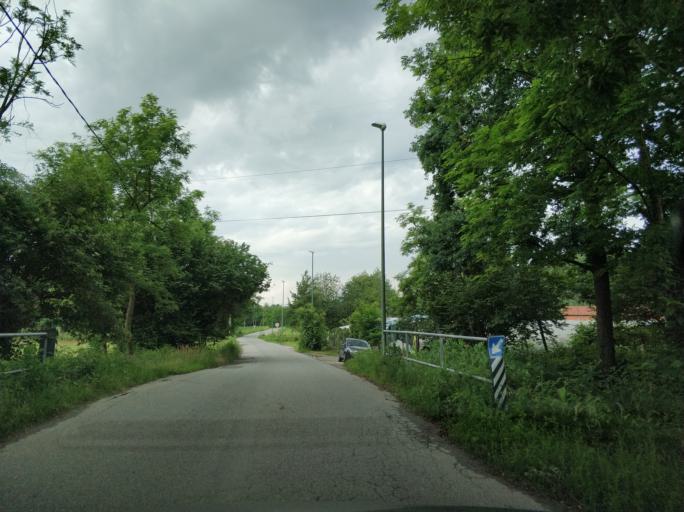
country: IT
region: Piedmont
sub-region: Provincia di Torino
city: San Maurizio
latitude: 45.1902
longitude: 7.6100
